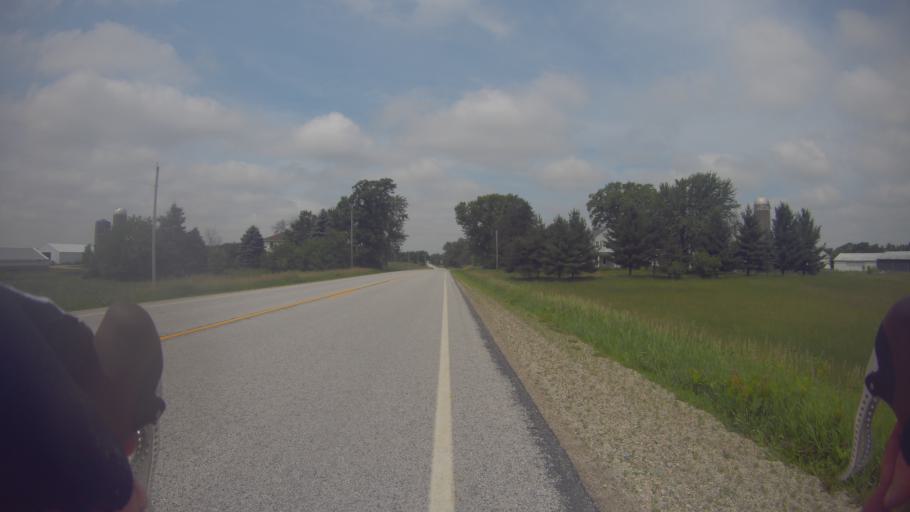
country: US
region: Wisconsin
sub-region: Jefferson County
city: Lake Ripley
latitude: 42.9498
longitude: -88.9898
